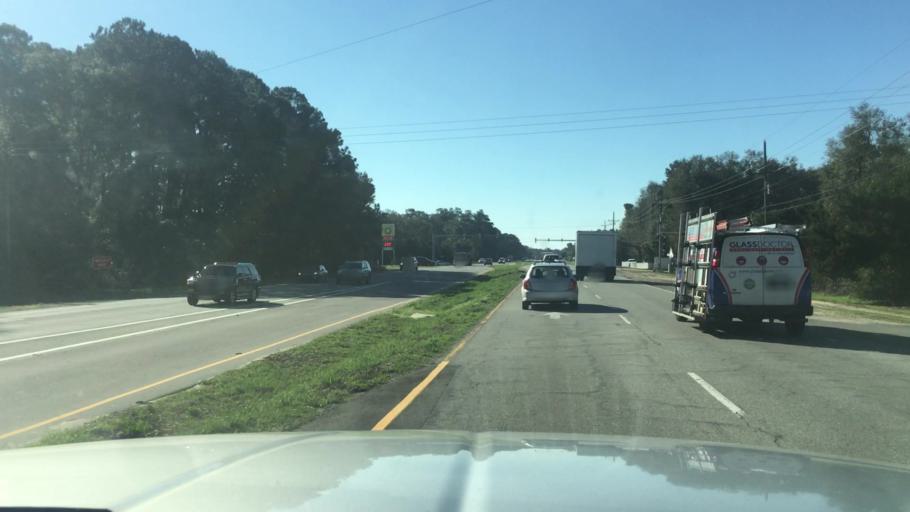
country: US
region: North Carolina
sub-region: New Hanover County
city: Sea Breeze
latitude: 34.0911
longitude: -77.8969
